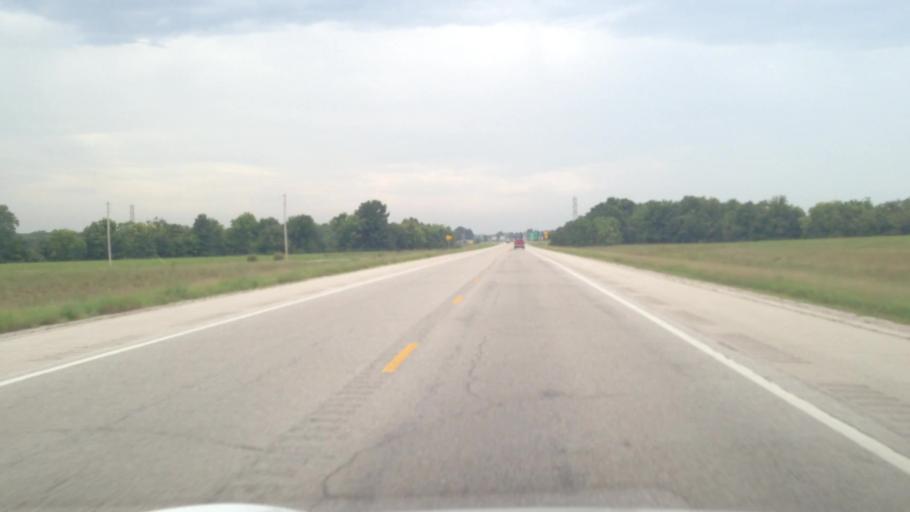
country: US
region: Kansas
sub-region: Cherokee County
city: Baxter Springs
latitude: 37.0810
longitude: -94.7097
